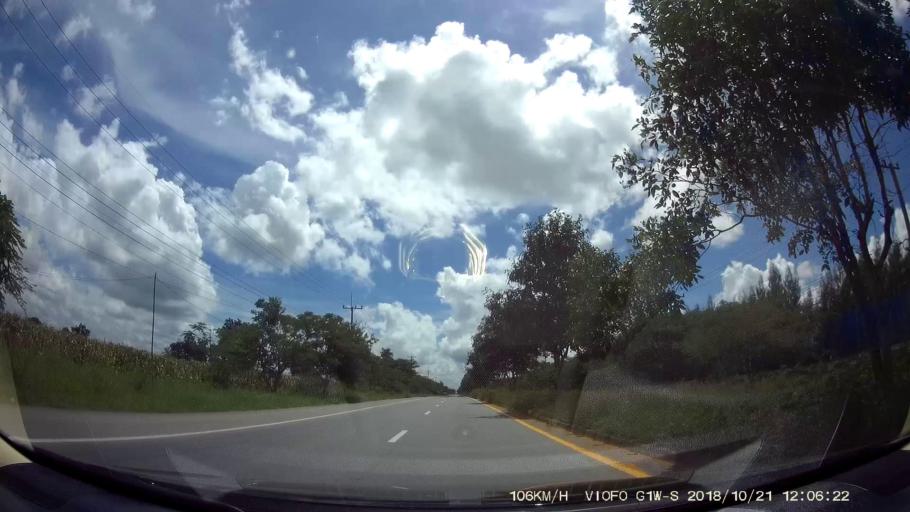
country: TH
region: Chaiyaphum
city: Chatturat
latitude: 15.4643
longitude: 101.8258
